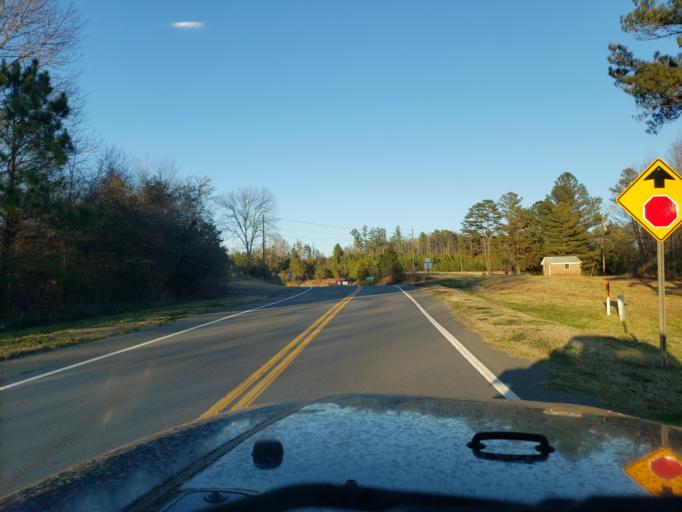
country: US
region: South Carolina
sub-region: Cherokee County
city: Blacksburg
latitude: 35.0746
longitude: -81.4363
